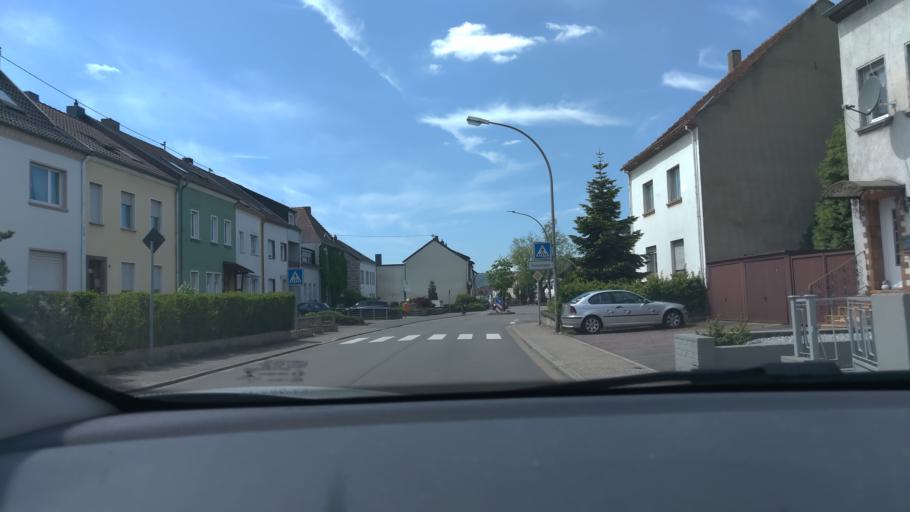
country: DE
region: Saarland
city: Saarlouis
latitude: 49.3344
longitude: 6.7515
